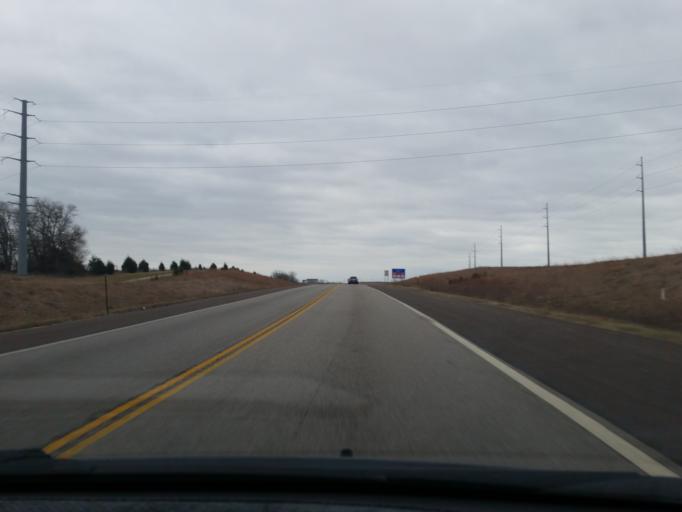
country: US
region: Kansas
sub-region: Douglas County
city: Lawrence
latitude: 38.9869
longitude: -95.3409
